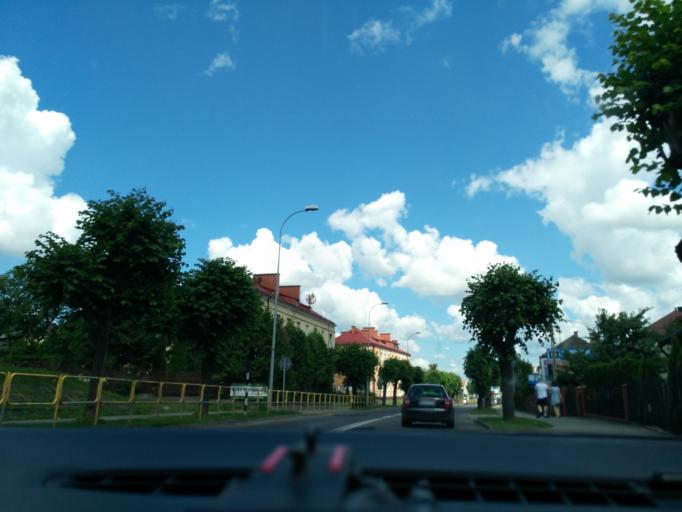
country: PL
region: Podlasie
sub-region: Powiat siemiatycki
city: Siemiatycze
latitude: 52.4253
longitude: 22.8647
